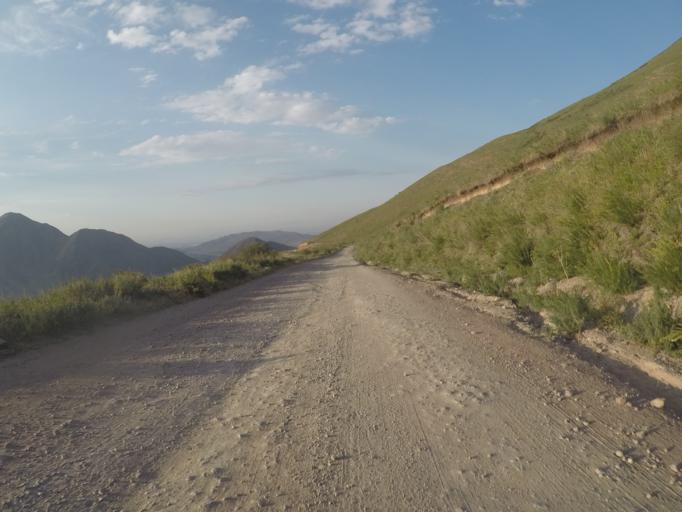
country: KG
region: Chuy
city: Bishkek
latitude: 42.6524
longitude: 74.6619
